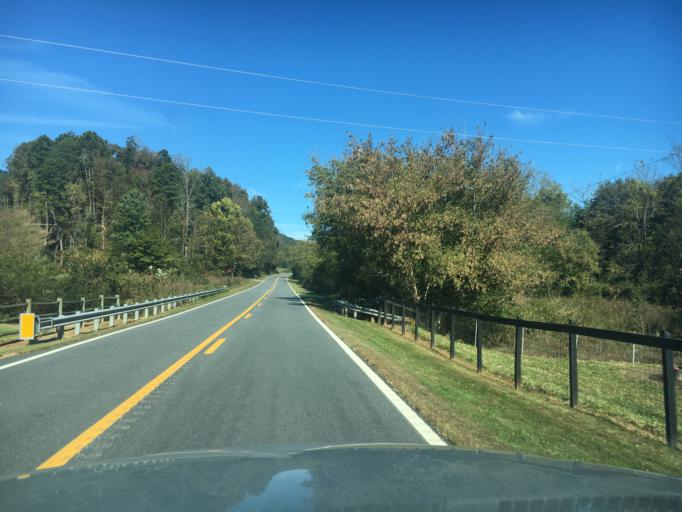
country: US
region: North Carolina
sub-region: Rutherford County
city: Spindale
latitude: 35.5260
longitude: -81.8555
